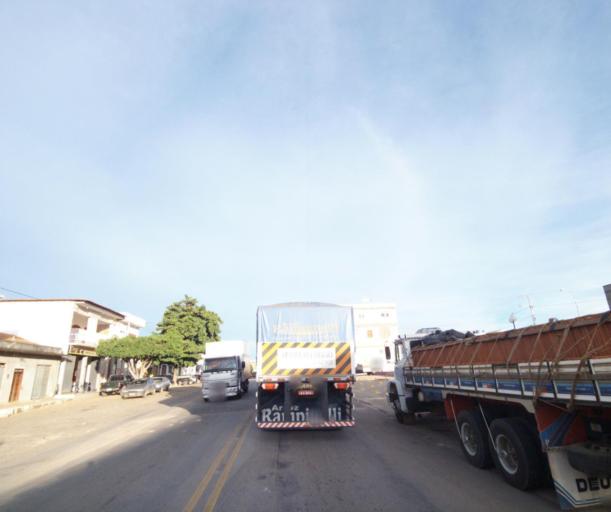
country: BR
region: Bahia
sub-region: Cacule
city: Cacule
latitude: -14.2056
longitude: -42.1147
